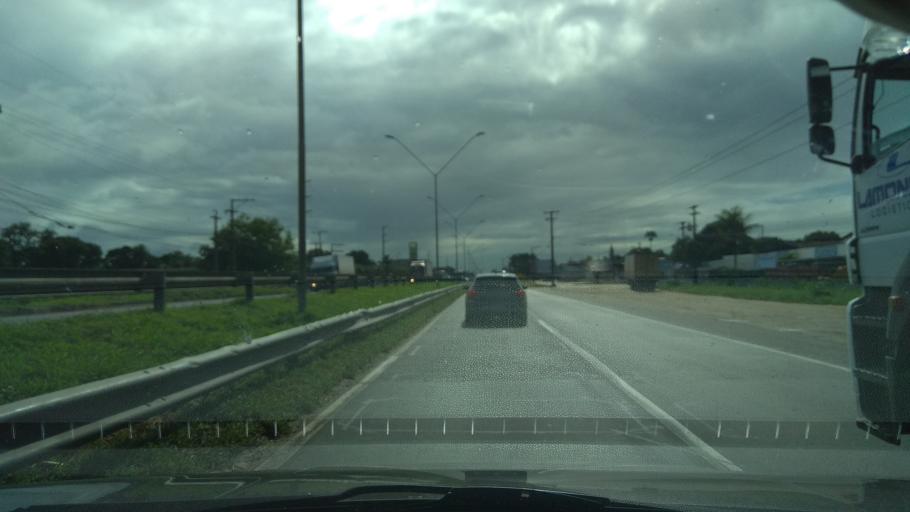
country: BR
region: Bahia
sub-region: Feira De Santana
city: Feira de Santana
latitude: -12.3097
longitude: -38.8860
